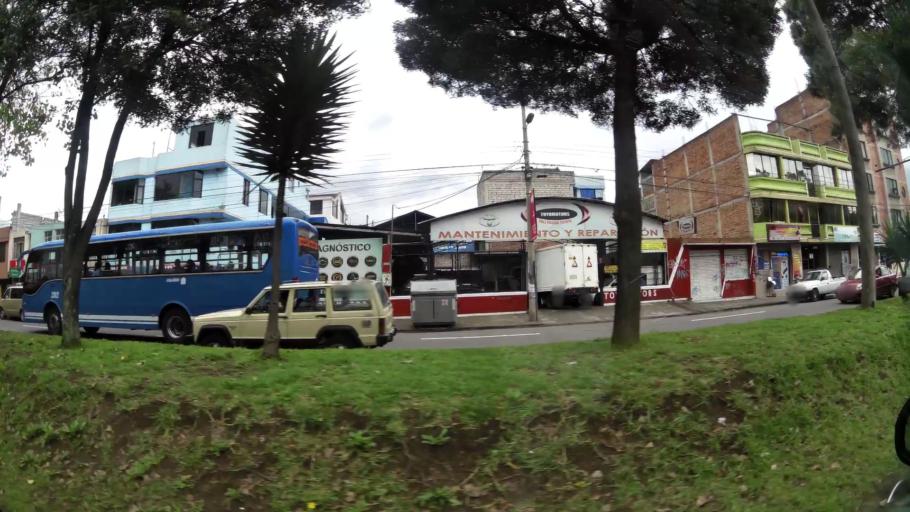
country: EC
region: Pichincha
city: Quito
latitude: -0.2812
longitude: -78.5479
